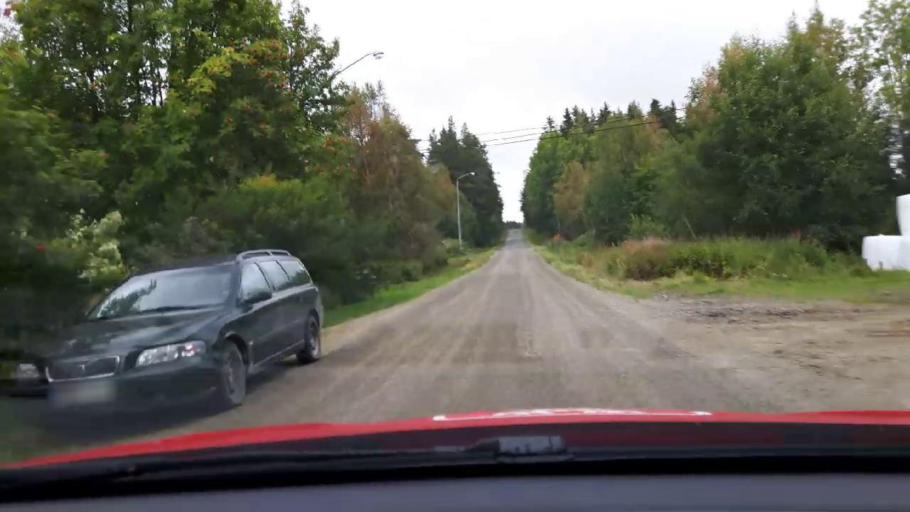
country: SE
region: Jaemtland
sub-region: Bergs Kommun
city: Hoverberg
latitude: 62.8627
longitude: 14.2971
